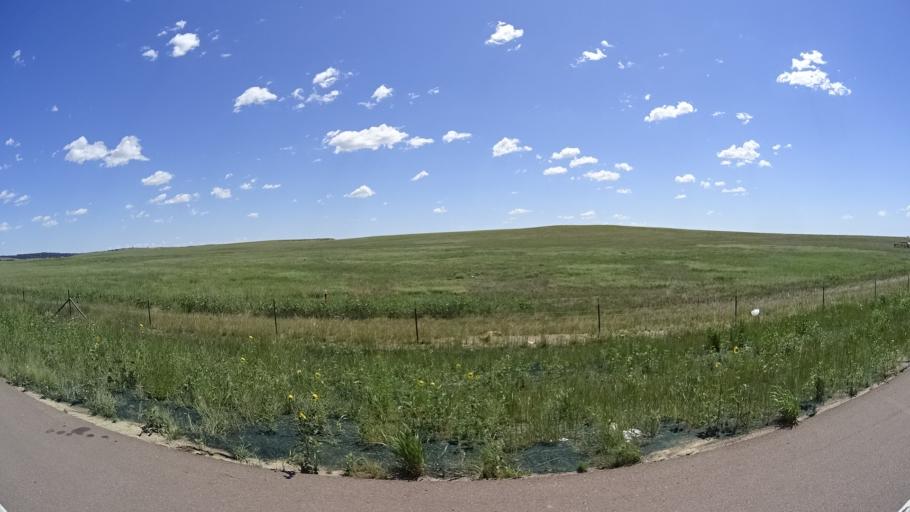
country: US
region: Colorado
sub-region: El Paso County
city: Cimarron Hills
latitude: 38.8254
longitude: -104.6826
